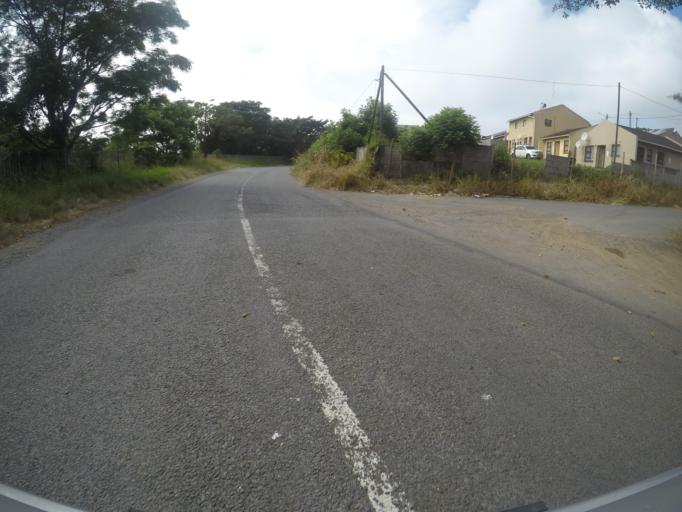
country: ZA
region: Eastern Cape
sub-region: Buffalo City Metropolitan Municipality
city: East London
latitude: -32.9983
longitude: 27.9114
